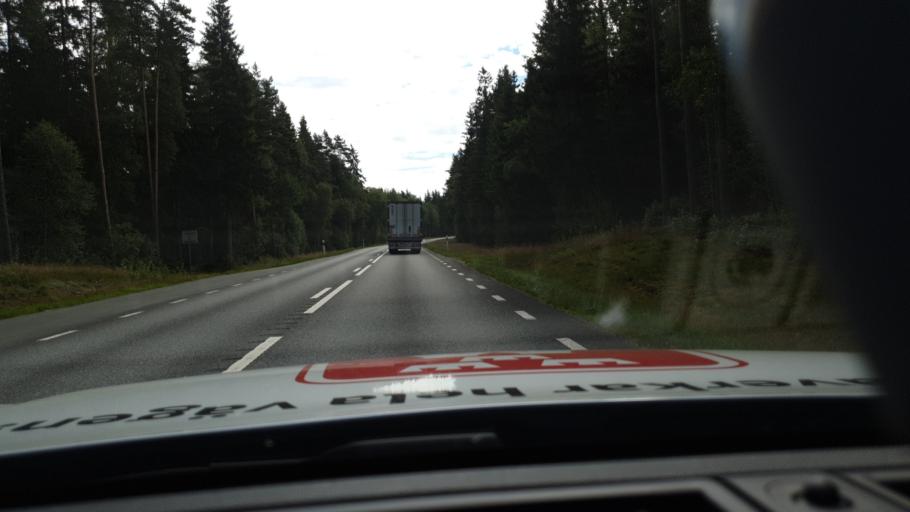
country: SE
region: Joenkoeping
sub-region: Savsjo Kommun
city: Vrigstad
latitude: 57.3873
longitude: 14.3925
